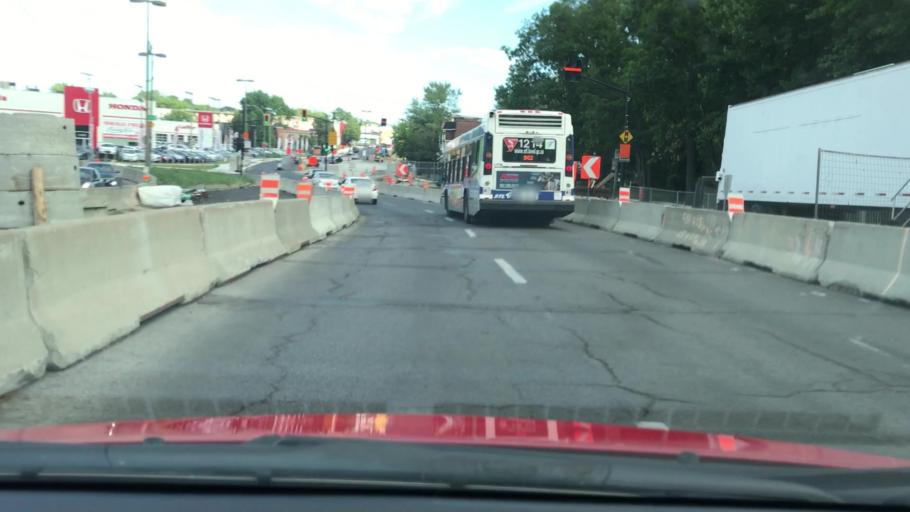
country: CA
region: Quebec
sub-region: Laval
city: Laval
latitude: 45.5318
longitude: -73.7268
